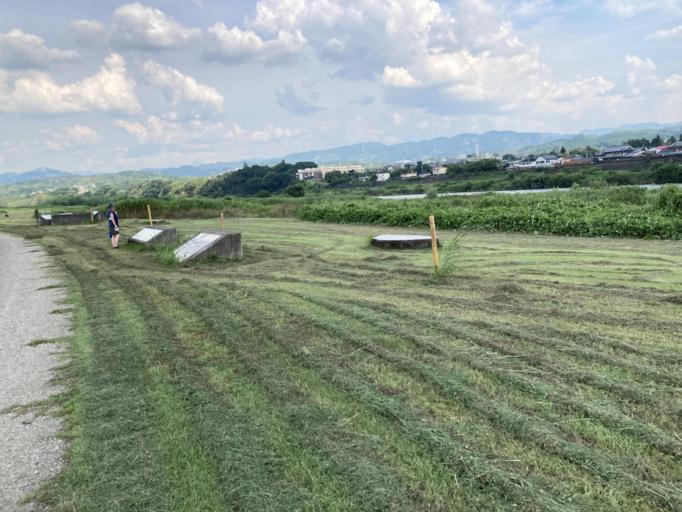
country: JP
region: Nara
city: Gojo
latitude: 34.3490
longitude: 135.6970
